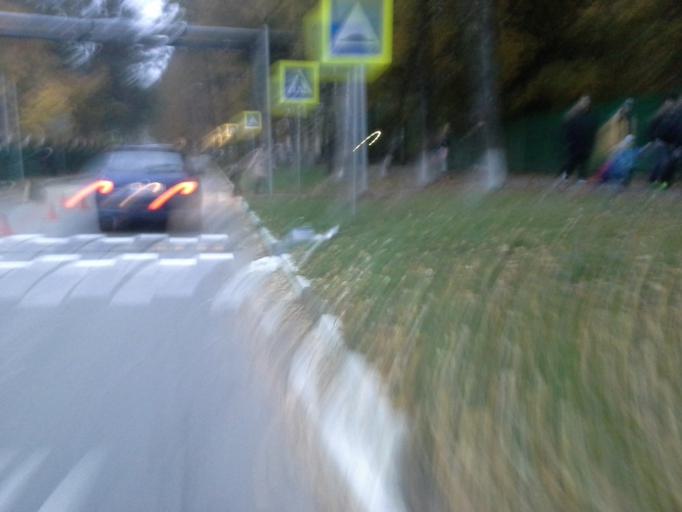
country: RU
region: Moskovskaya
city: Nazar'yevo
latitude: 55.7022
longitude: 37.0263
